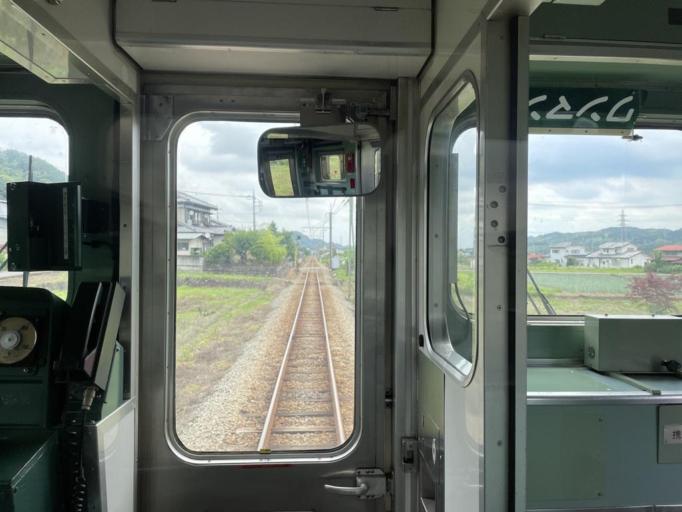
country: JP
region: Gunma
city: Tomioka
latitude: 36.2335
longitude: 138.8051
